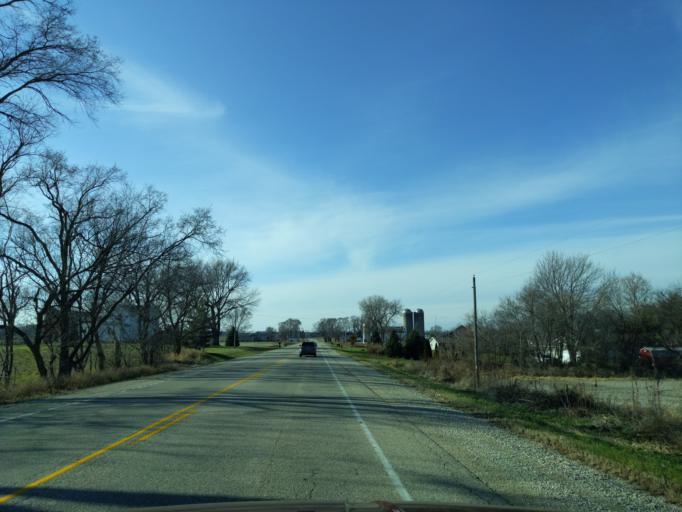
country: US
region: Wisconsin
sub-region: Rock County
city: Milton
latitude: 42.8247
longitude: -88.9698
